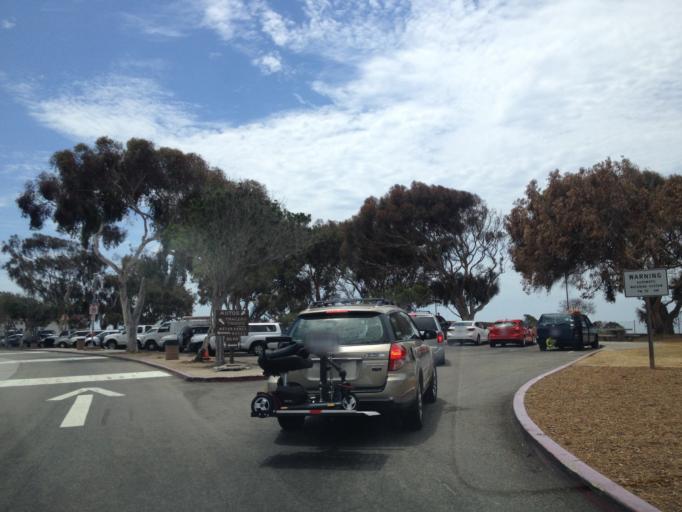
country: US
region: California
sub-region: San Diego County
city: Camp Pendleton South
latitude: 33.2736
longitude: -117.4445
